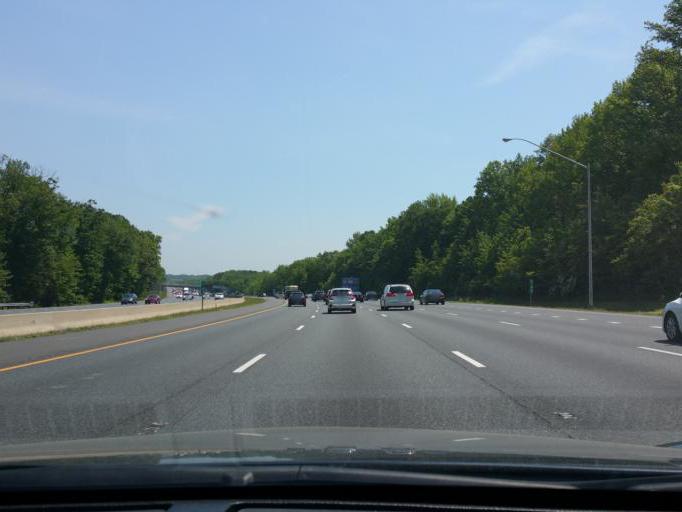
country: US
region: Maryland
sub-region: Harford County
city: Joppatowne
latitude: 39.4422
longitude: -76.3432
